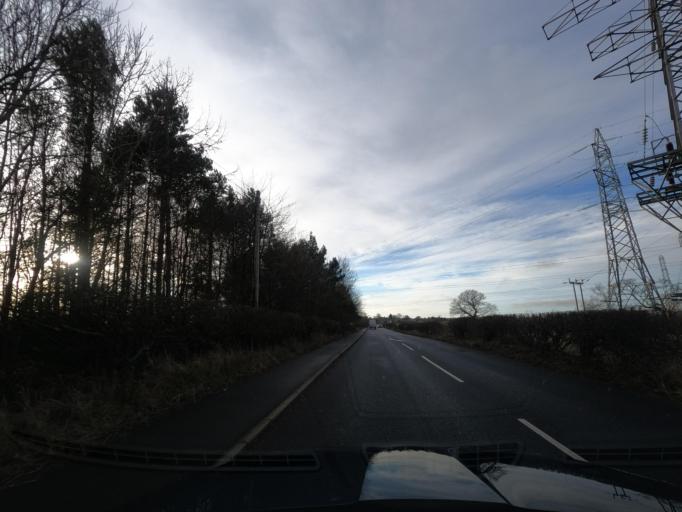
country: GB
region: England
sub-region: Northumberland
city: Bedlington
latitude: 55.1245
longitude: -1.5687
